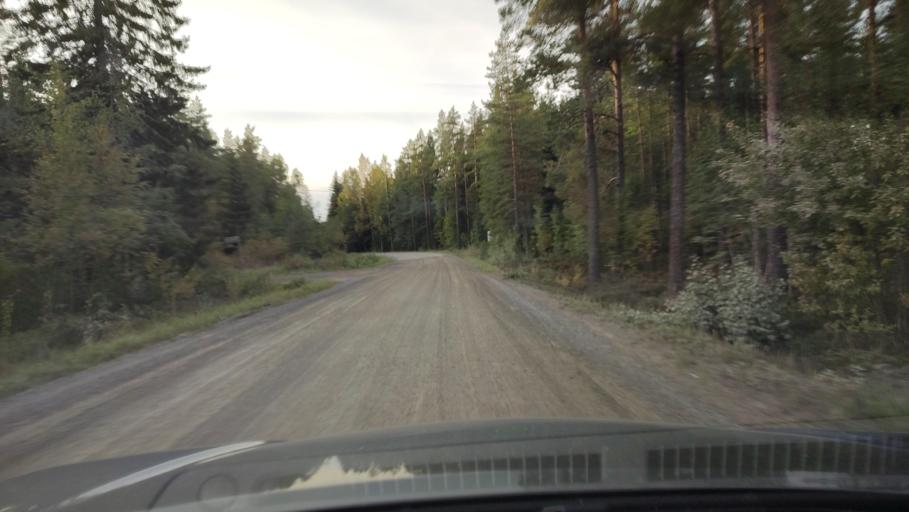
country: FI
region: Southern Ostrobothnia
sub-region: Suupohja
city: Karijoki
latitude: 62.1251
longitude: 21.5966
